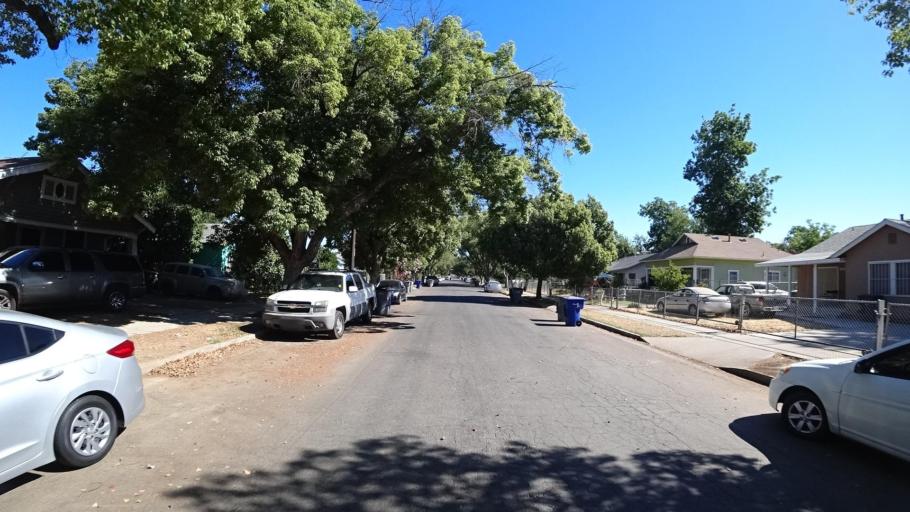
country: US
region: California
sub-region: Fresno County
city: Fresno
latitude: 36.7164
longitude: -119.7886
